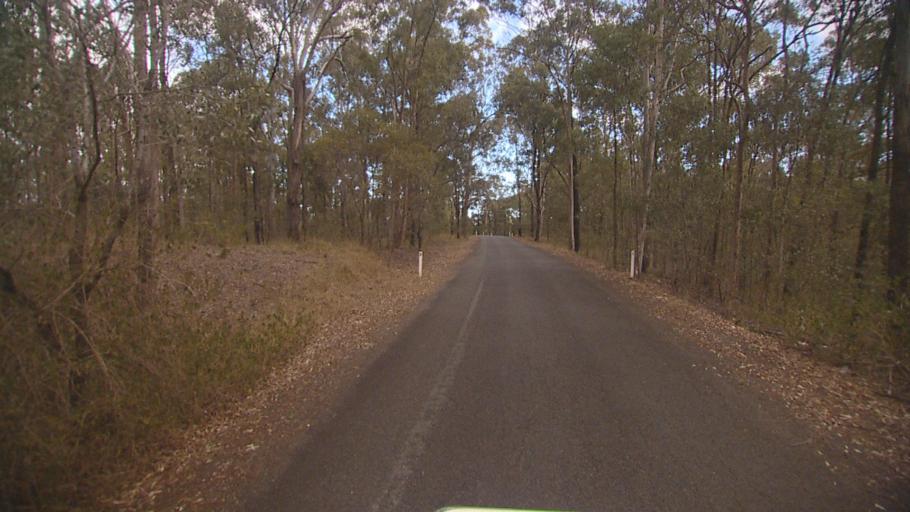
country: AU
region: Queensland
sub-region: Logan
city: Cedar Vale
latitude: -27.9016
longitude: 153.0330
